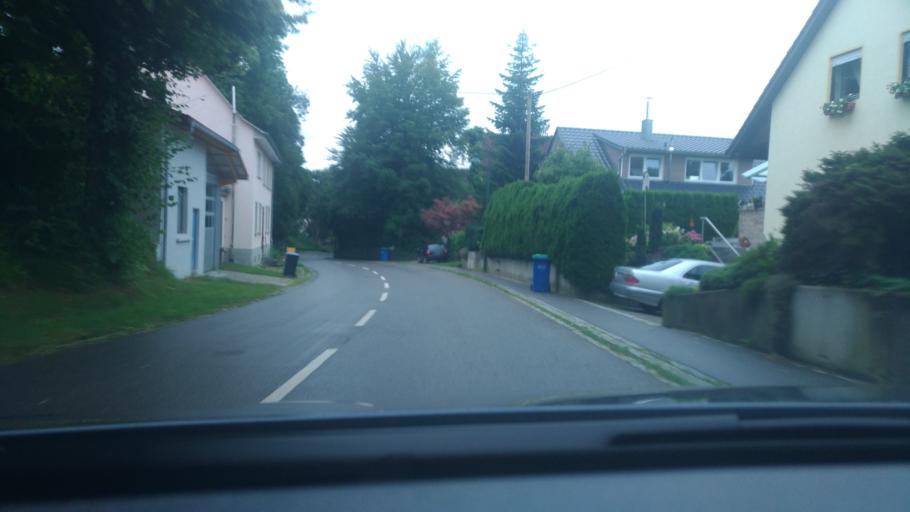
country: DE
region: Baden-Wuerttemberg
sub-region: Tuebingen Region
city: Sipplingen
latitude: 47.8325
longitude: 9.0954
